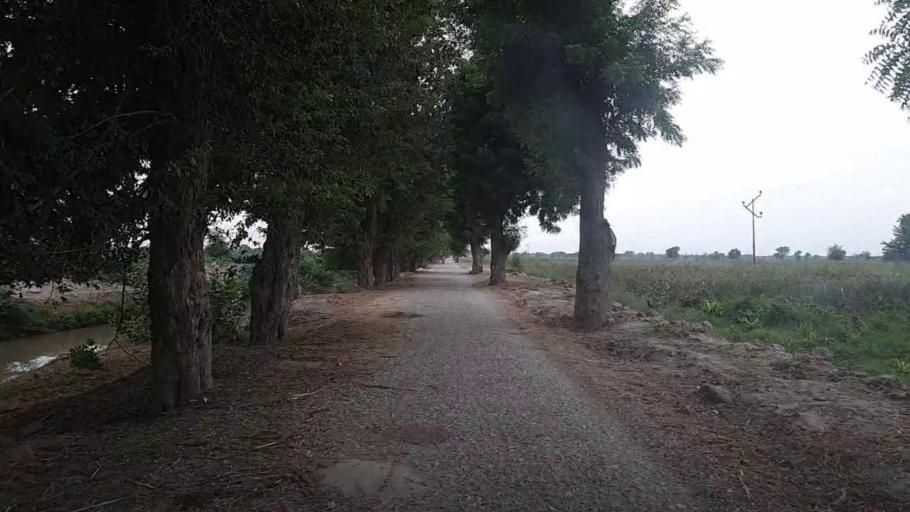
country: PK
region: Sindh
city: Karaundi
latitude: 26.9605
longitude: 68.3655
